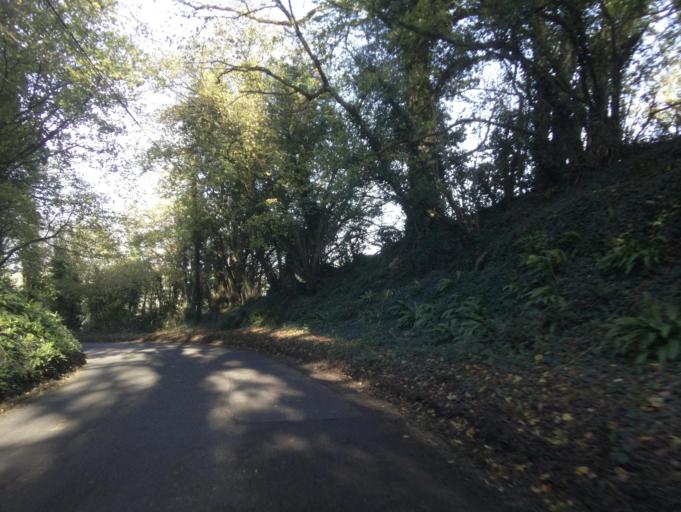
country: GB
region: England
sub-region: Somerset
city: Bruton
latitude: 51.0877
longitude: -2.4622
